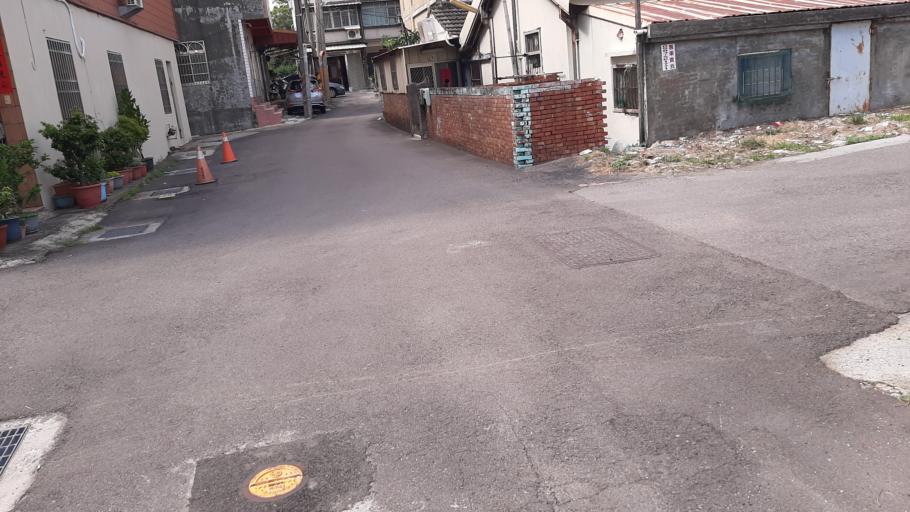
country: TW
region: Taiwan
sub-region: Changhua
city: Chang-hua
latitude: 24.2123
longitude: 120.5482
